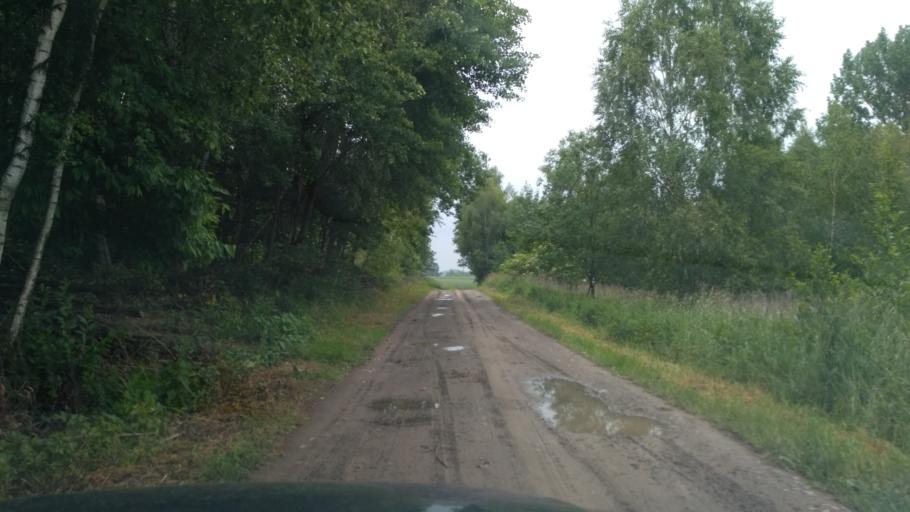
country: PL
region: Subcarpathian Voivodeship
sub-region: Powiat ropczycko-sedziszowski
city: Zagorzyce
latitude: 49.9833
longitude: 21.7070
